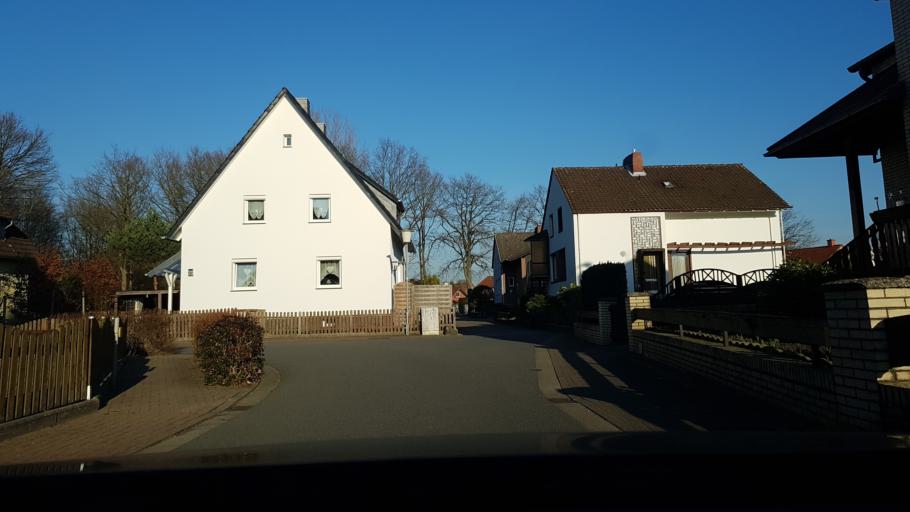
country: DE
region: Lower Saxony
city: Gifhorn
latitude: 52.5060
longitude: 10.5776
